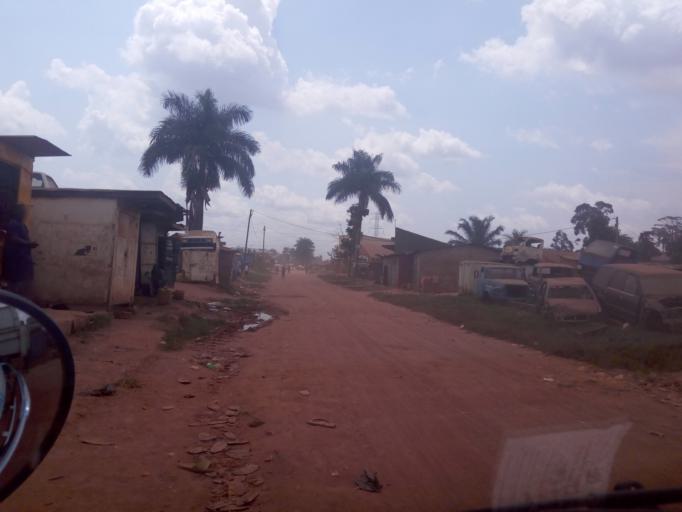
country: UG
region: Central Region
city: Kampala Central Division
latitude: 0.3455
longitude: 32.5571
